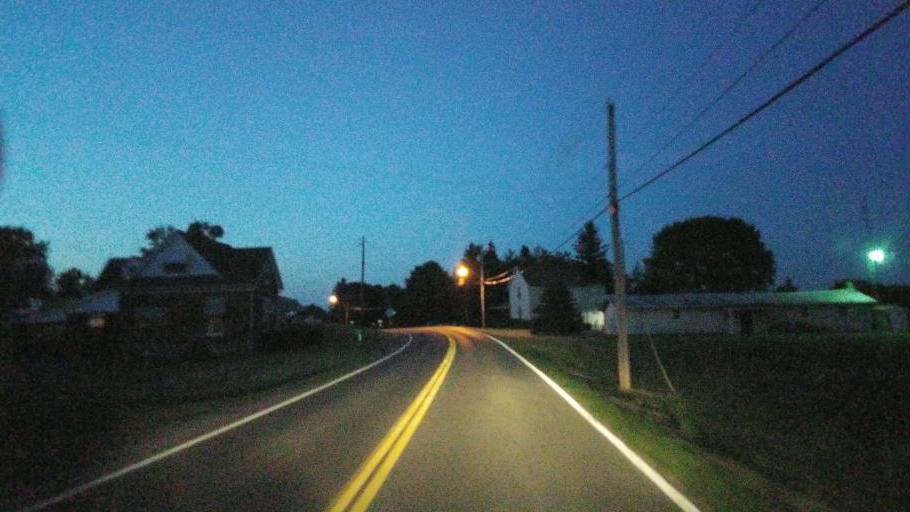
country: US
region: Ohio
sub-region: Highland County
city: Greenfield
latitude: 39.3427
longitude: -83.3908
